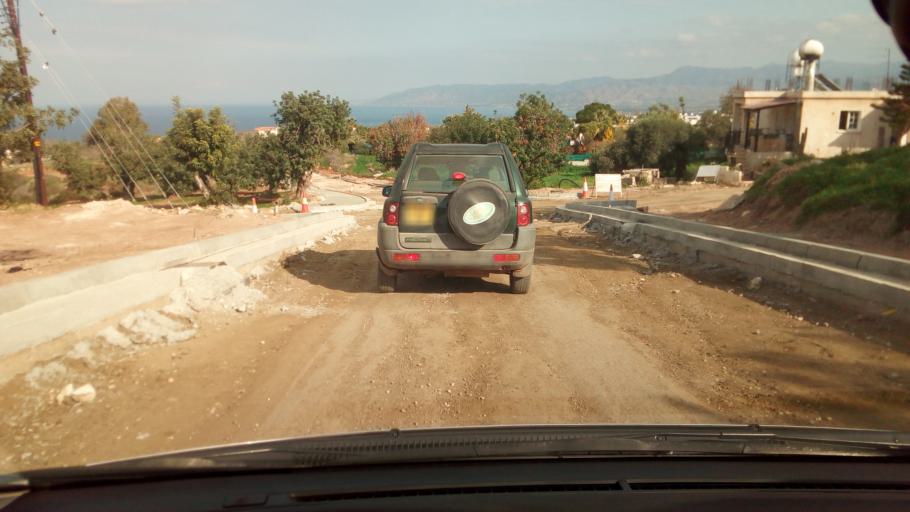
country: CY
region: Pafos
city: Polis
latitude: 35.0253
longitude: 32.3598
